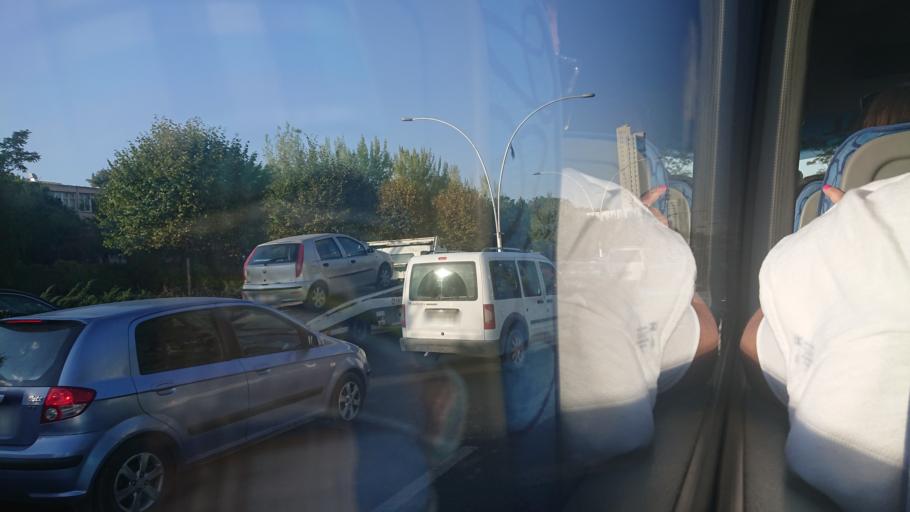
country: TR
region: Ankara
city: Ankara
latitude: 39.9341
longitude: 32.8216
